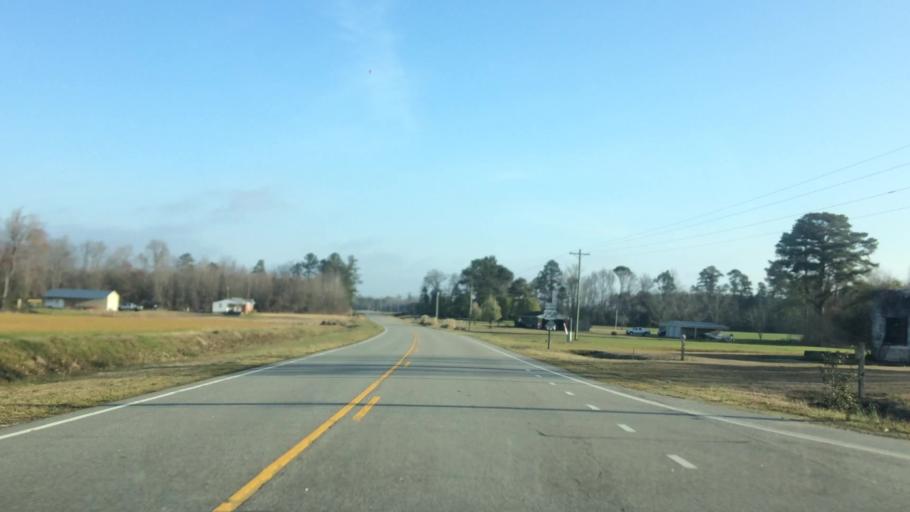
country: US
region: North Carolina
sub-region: Edgecombe County
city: Pinetops
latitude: 35.7046
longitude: -77.6334
